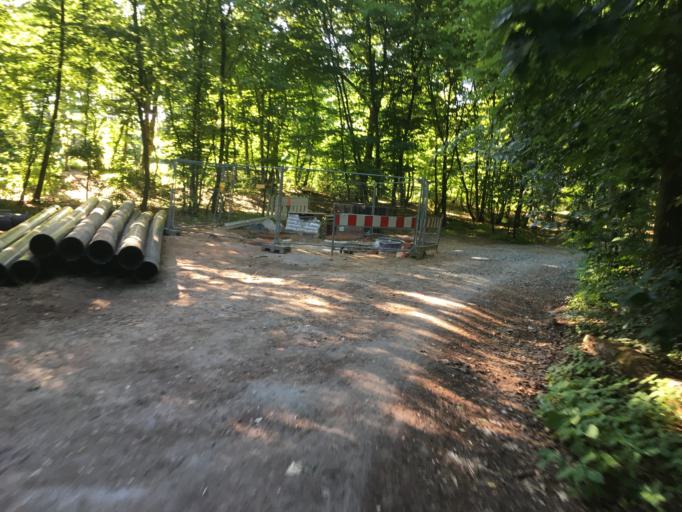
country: DE
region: Hesse
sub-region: Regierungsbezirk Darmstadt
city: Neu Isenburg
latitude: 50.0571
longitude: 8.6671
